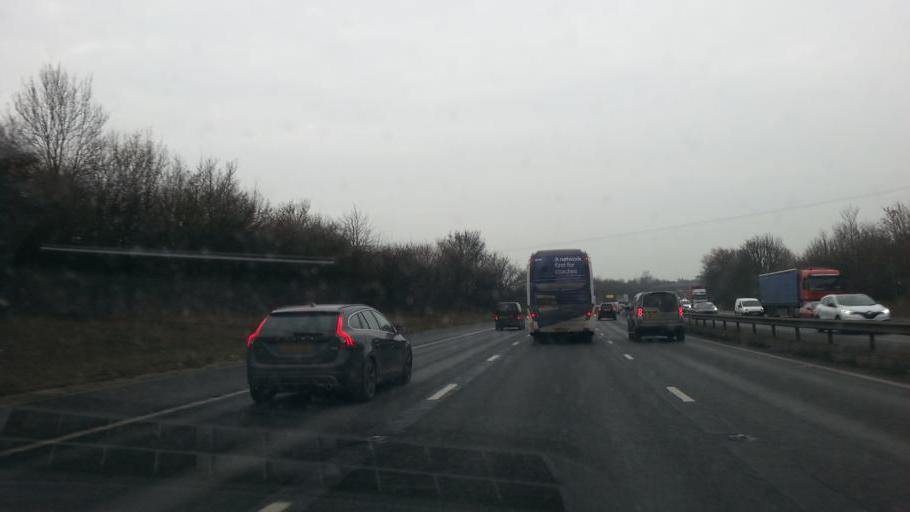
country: GB
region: England
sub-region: Essex
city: Little Hallingbury
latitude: 51.8058
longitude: 0.1762
